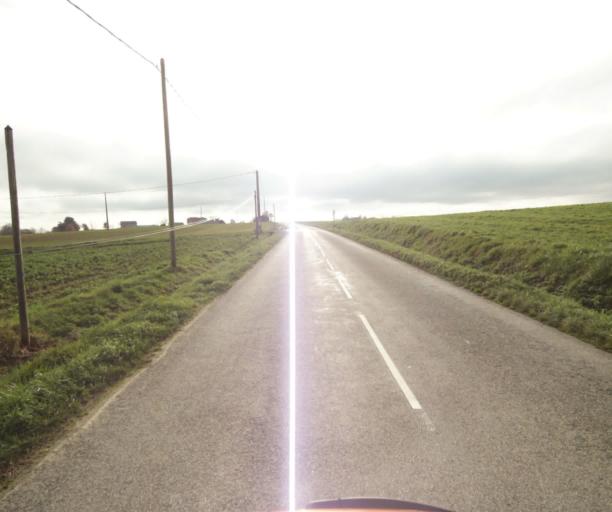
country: FR
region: Languedoc-Roussillon
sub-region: Departement de l'Aude
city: Belpech
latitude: 43.1910
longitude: 1.7269
